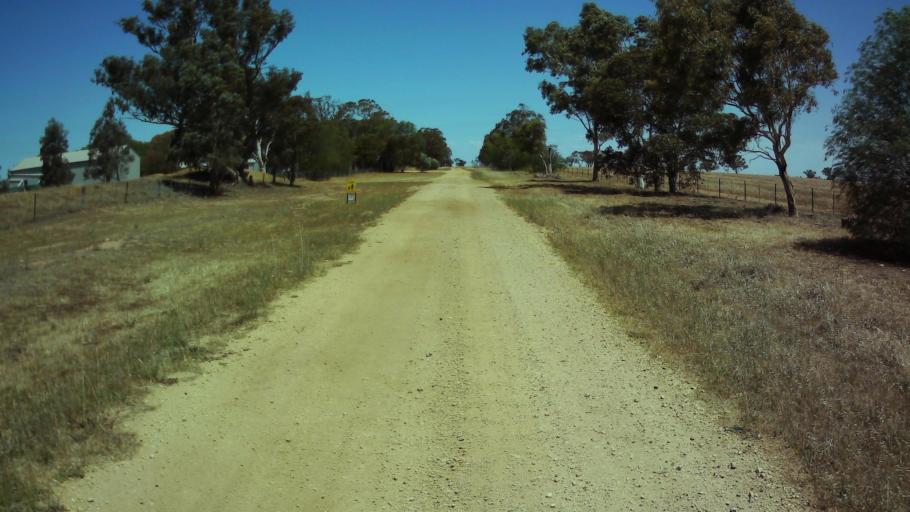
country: AU
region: New South Wales
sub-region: Weddin
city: Grenfell
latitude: -34.0182
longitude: 148.3514
